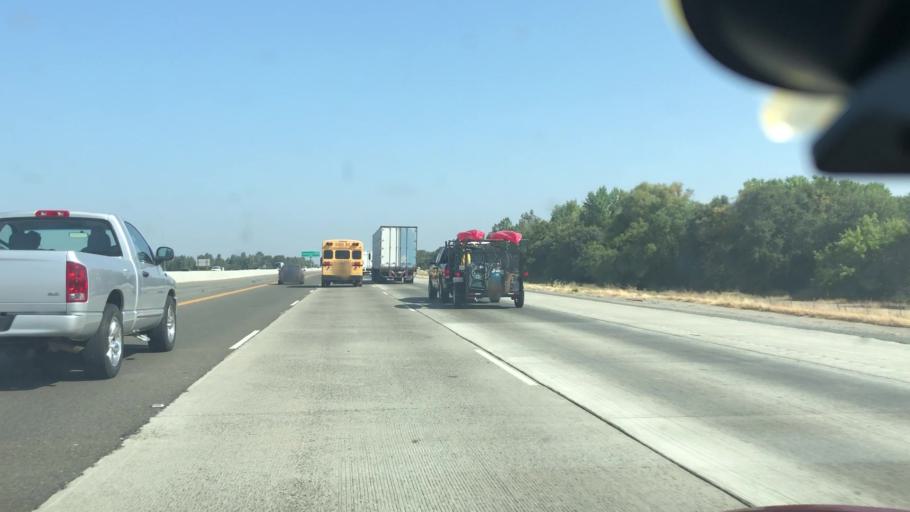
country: US
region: California
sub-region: Sacramento County
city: Parkway
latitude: 38.4437
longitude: -121.4909
